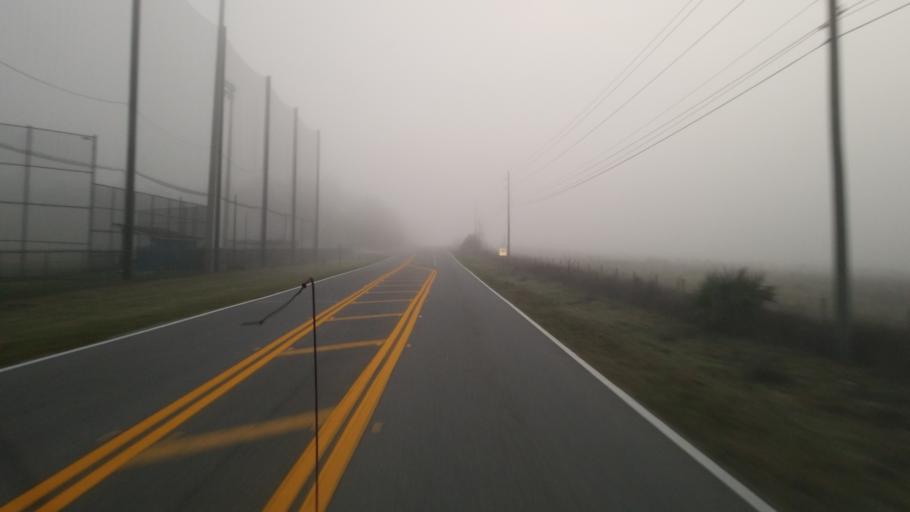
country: US
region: Florida
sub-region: Marion County
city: Ocala
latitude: 29.1502
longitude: -82.2494
